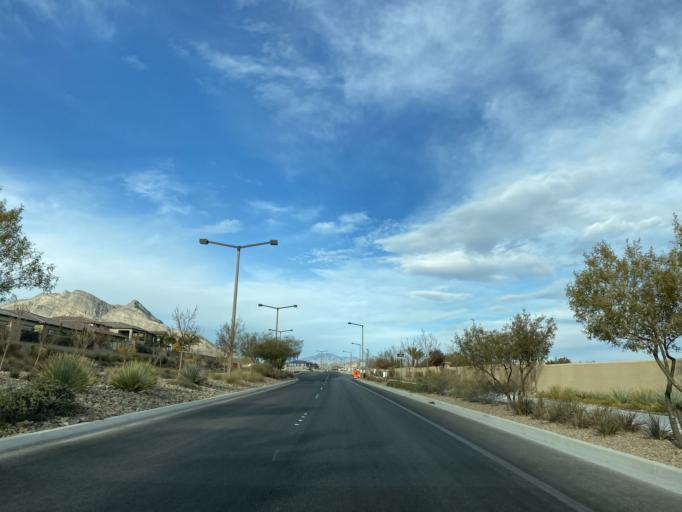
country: US
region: Nevada
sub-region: Clark County
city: Summerlin South
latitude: 36.1795
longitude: -115.3539
